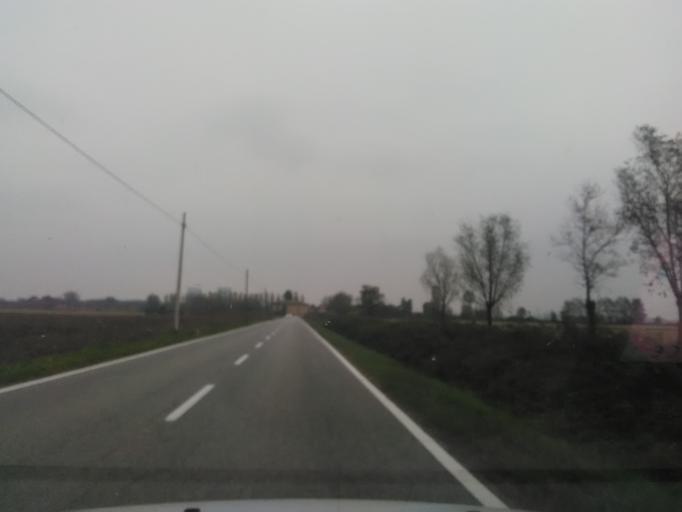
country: IT
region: Piedmont
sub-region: Provincia di Vercelli
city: Bianze
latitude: 45.2570
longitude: 8.1618
